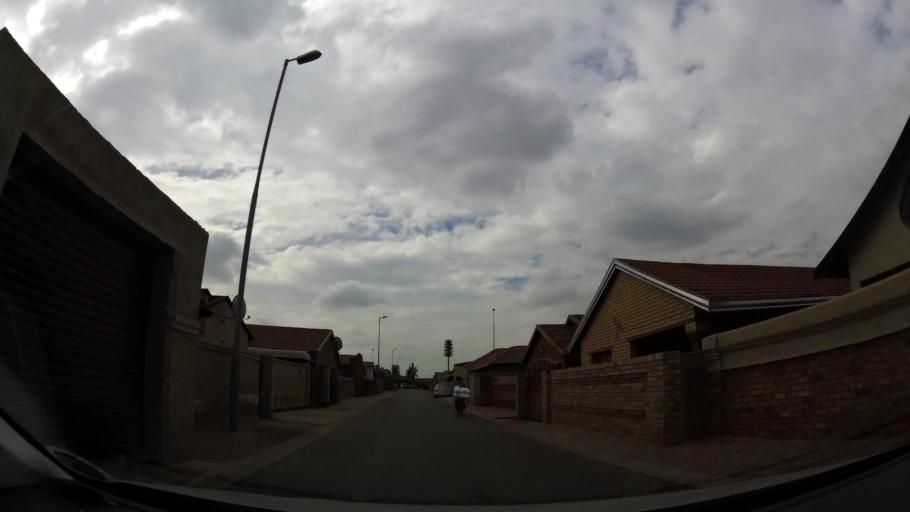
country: ZA
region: Gauteng
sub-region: City of Johannesburg Metropolitan Municipality
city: Soweto
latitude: -26.2744
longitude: 27.8560
